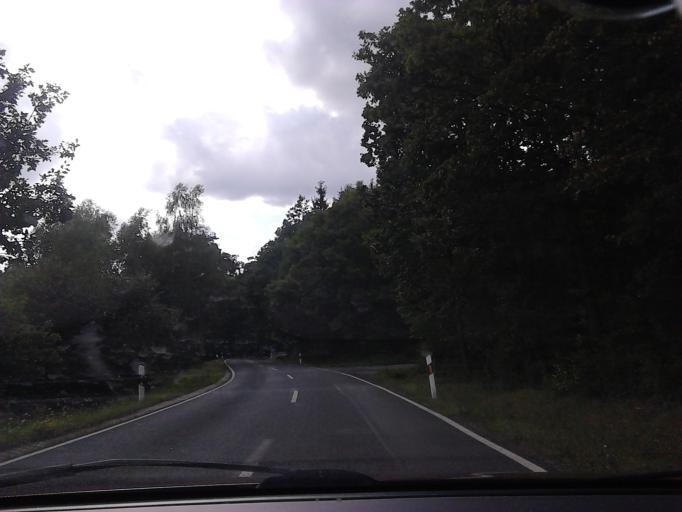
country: DE
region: Bavaria
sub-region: Upper Franconia
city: Weitramsdorf
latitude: 50.2741
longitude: 10.7860
